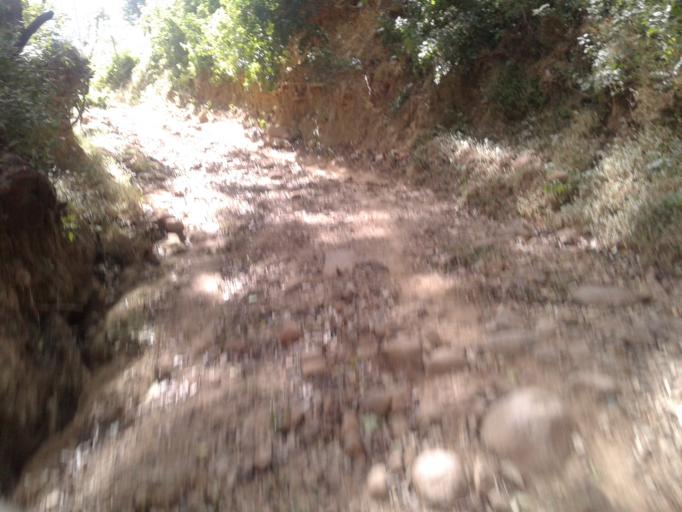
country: NI
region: Carazo
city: Santa Teresa
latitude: 11.6147
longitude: -86.1819
